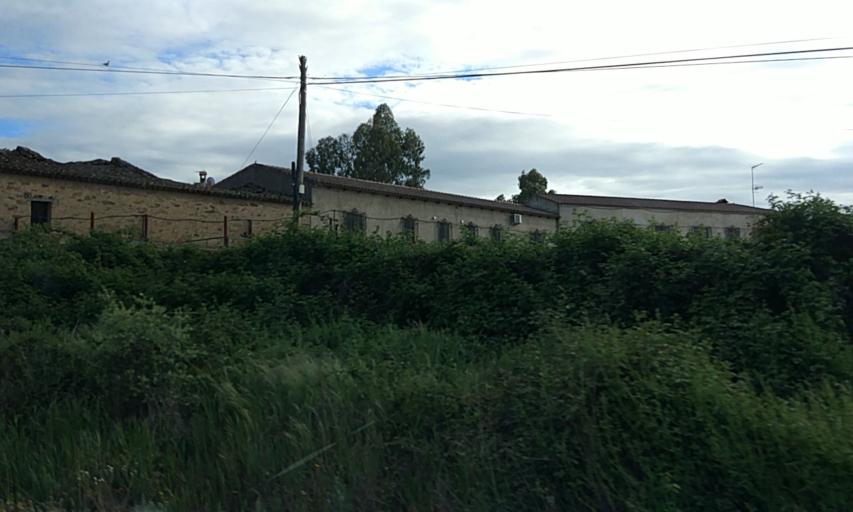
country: ES
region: Extremadura
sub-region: Provincia de Caceres
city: Huelaga
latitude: 40.0363
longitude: -6.6269
